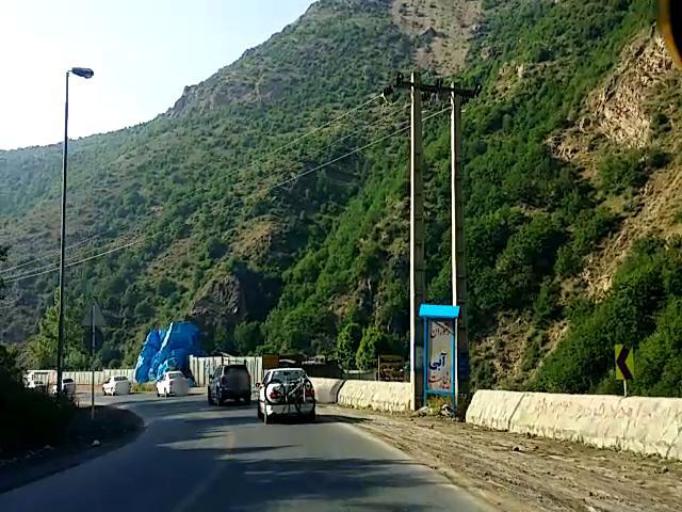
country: IR
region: Tehran
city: Tajrish
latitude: 36.2097
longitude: 51.3298
